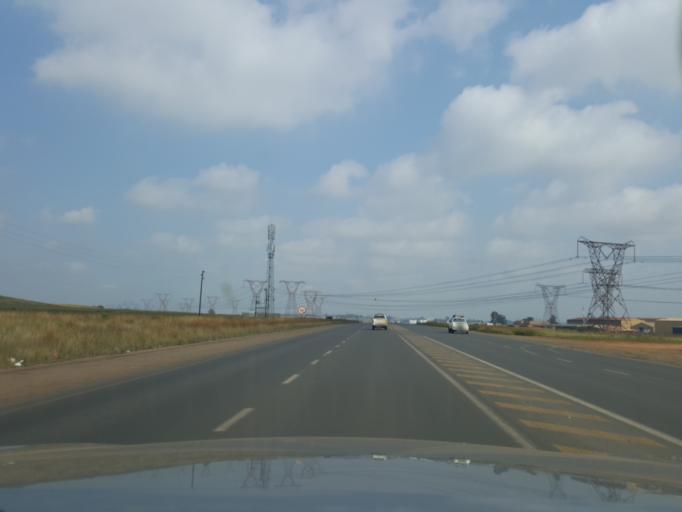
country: ZA
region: Mpumalanga
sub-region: Nkangala District Municipality
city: Witbank
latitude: -25.9740
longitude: 29.2748
